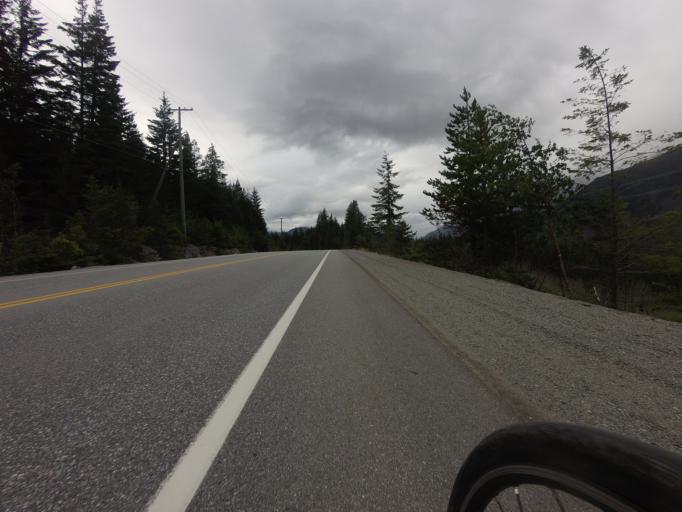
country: CA
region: British Columbia
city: Whistler
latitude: 50.1912
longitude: -122.8772
